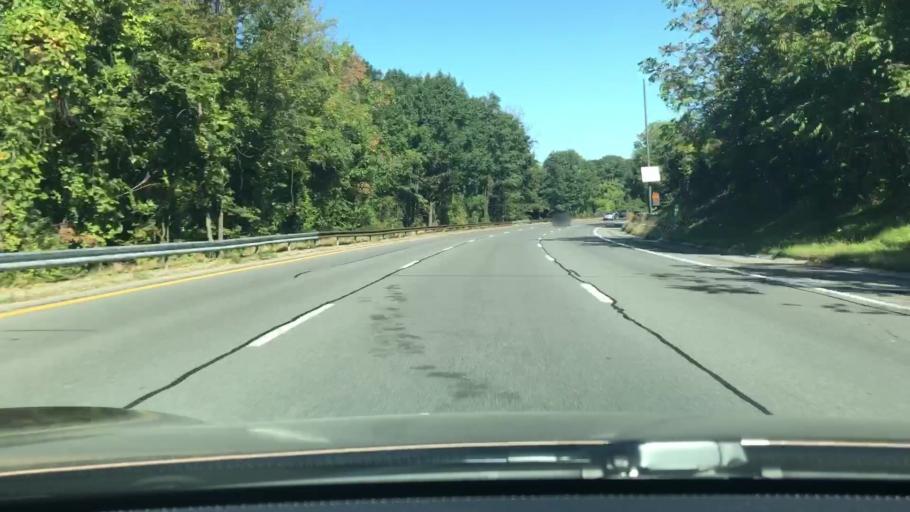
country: US
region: New York
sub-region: Westchester County
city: Tuckahoe
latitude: 40.9680
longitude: -73.8495
